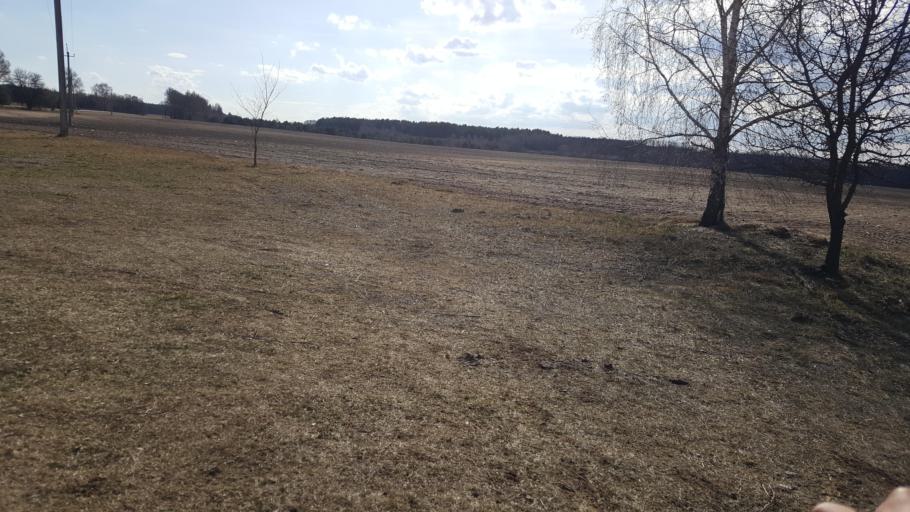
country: BY
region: Brest
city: Kamyanyets
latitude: 52.4159
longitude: 23.9219
